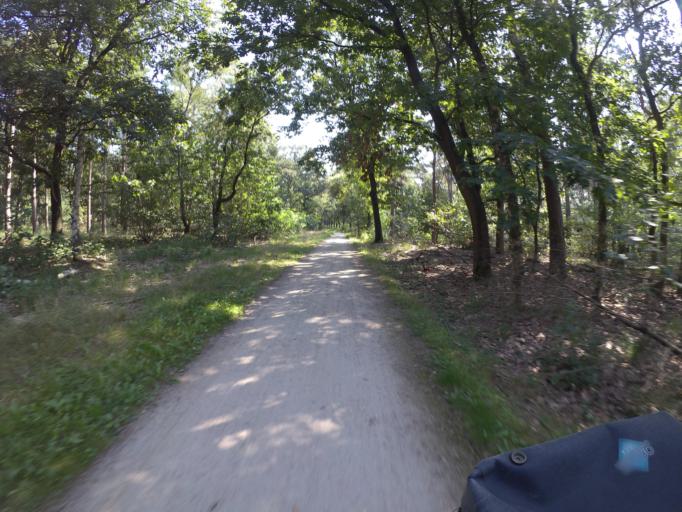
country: NL
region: North Brabant
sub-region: Gemeente Mill en Sint Hubert
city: Wilbertoord
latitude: 51.6193
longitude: 5.8140
